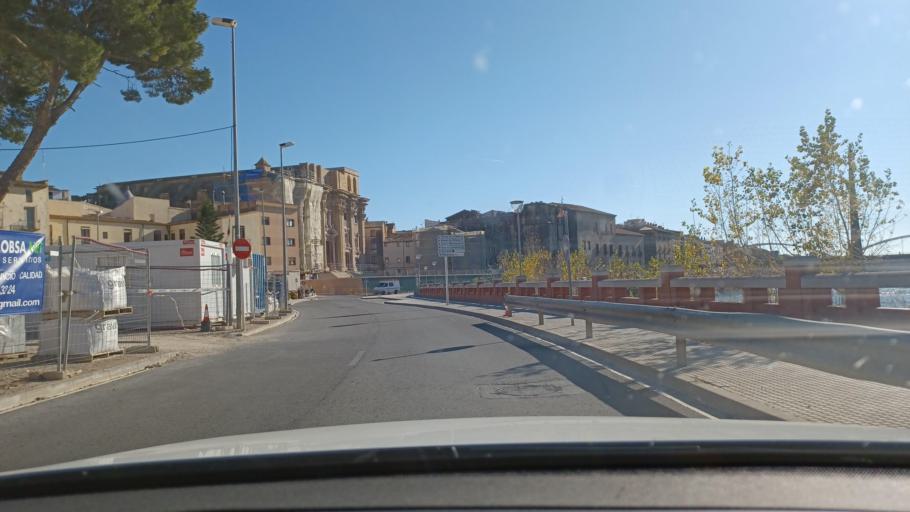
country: ES
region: Catalonia
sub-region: Provincia de Tarragona
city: Tortosa
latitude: 40.8157
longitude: 0.5213
